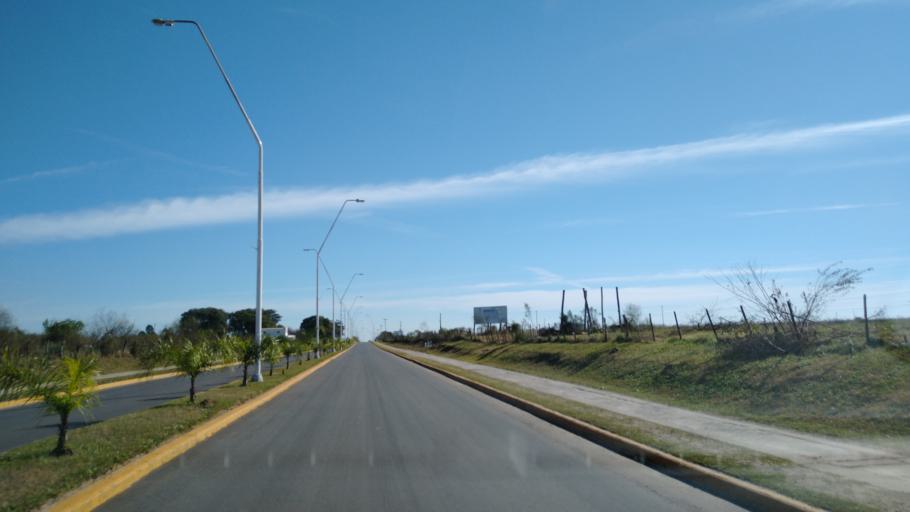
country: AR
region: Entre Rios
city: Chajari
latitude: -30.7560
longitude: -58.0025
